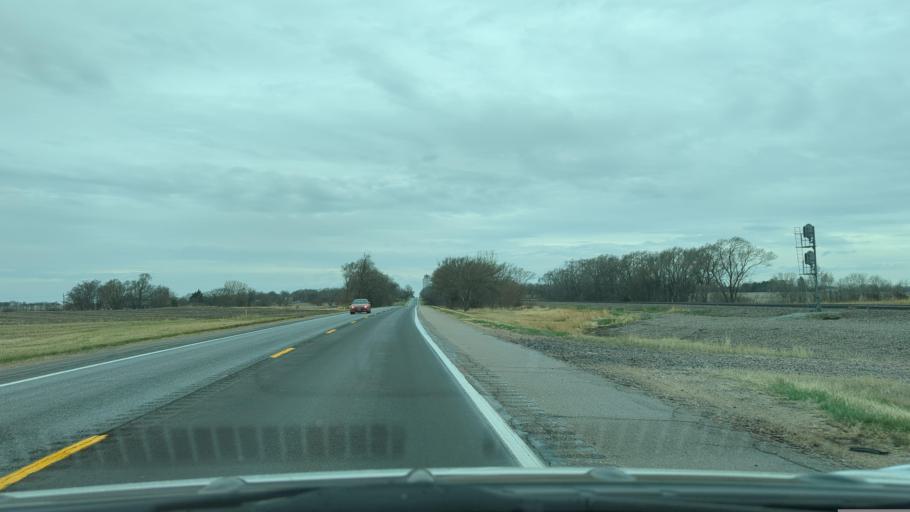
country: US
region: Nebraska
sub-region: Saunders County
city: Ashland
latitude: 40.9730
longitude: -96.4309
